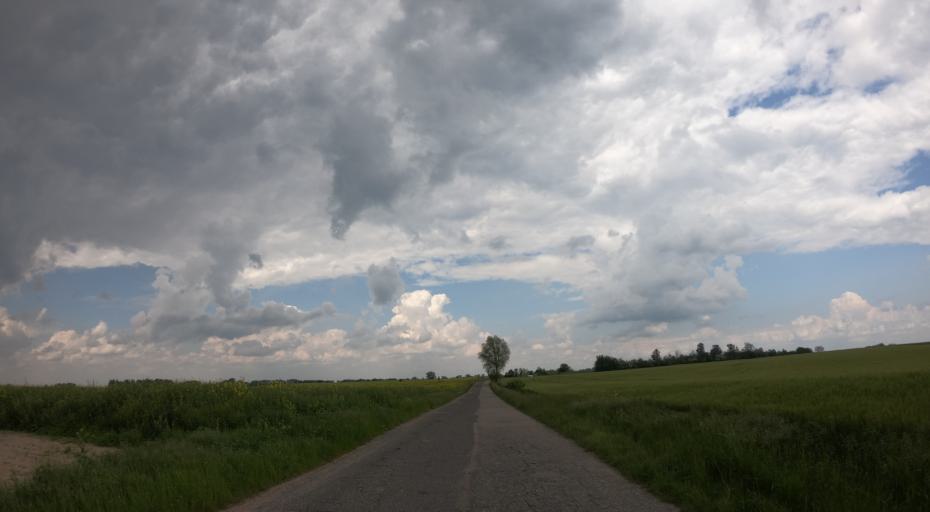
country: PL
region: West Pomeranian Voivodeship
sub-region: Powiat pyrzycki
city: Kozielice
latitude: 53.1574
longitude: 14.7967
